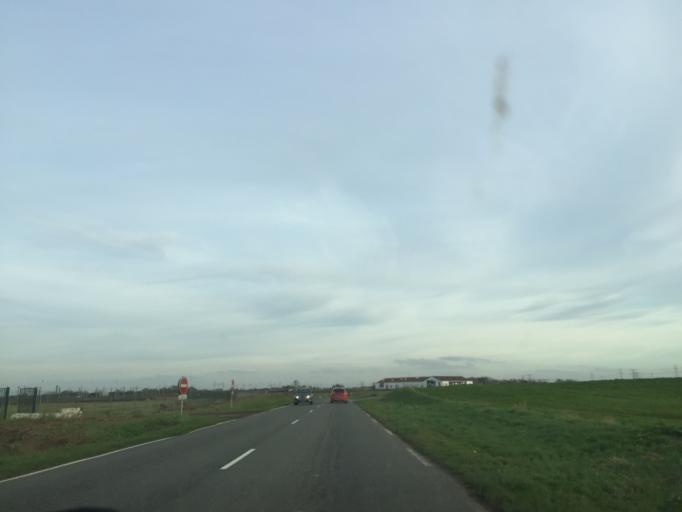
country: FR
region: Nord-Pas-de-Calais
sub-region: Departement du Pas-de-Calais
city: Coquelles
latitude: 50.9132
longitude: 1.7934
